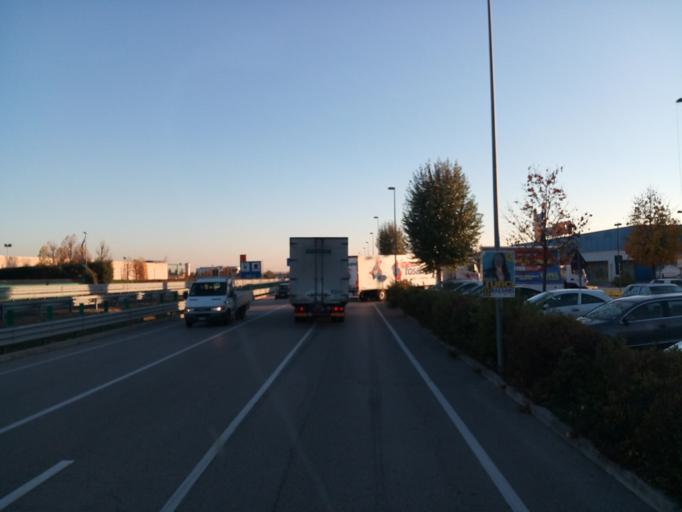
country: IT
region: Veneto
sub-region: Provincia di Vicenza
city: San Zeno-San Giuseppe
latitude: 45.7672
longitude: 11.7668
